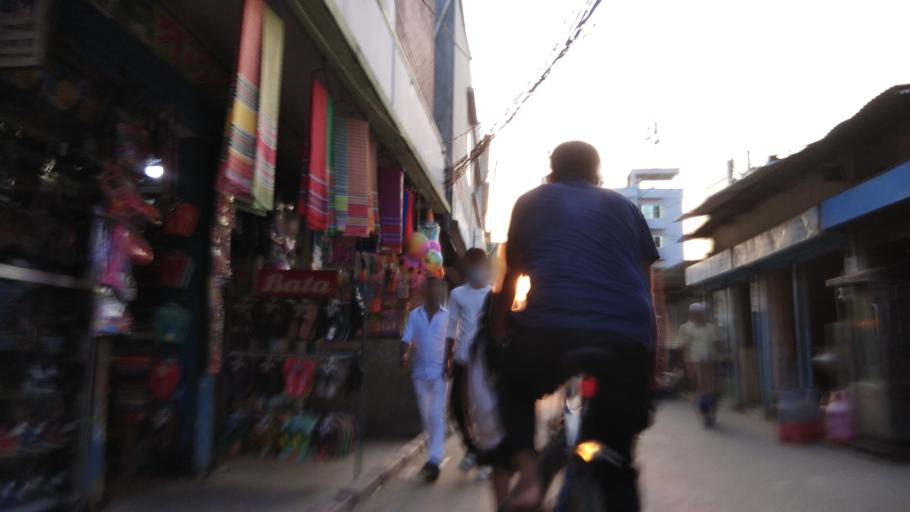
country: BD
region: Dhaka
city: Azimpur
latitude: 23.7983
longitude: 90.3377
